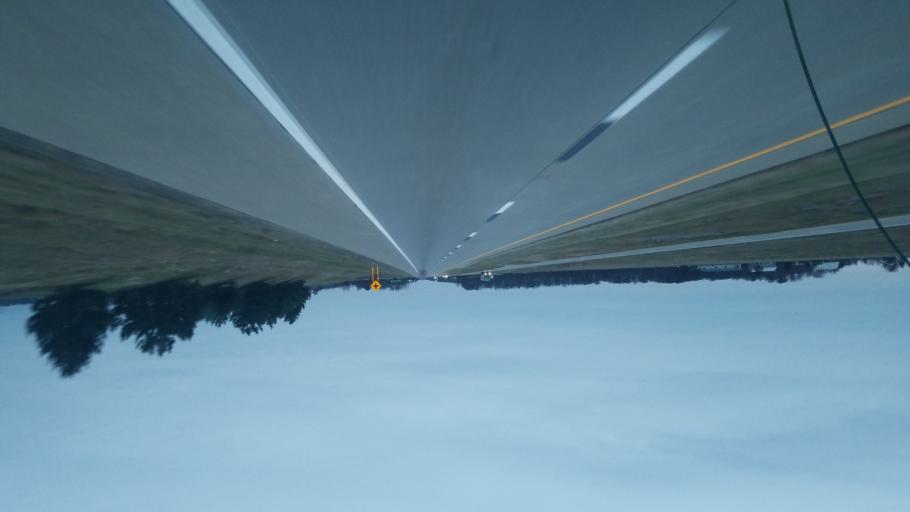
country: US
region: Ohio
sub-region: Hardin County
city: Ada
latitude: 40.8276
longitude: -83.8368
